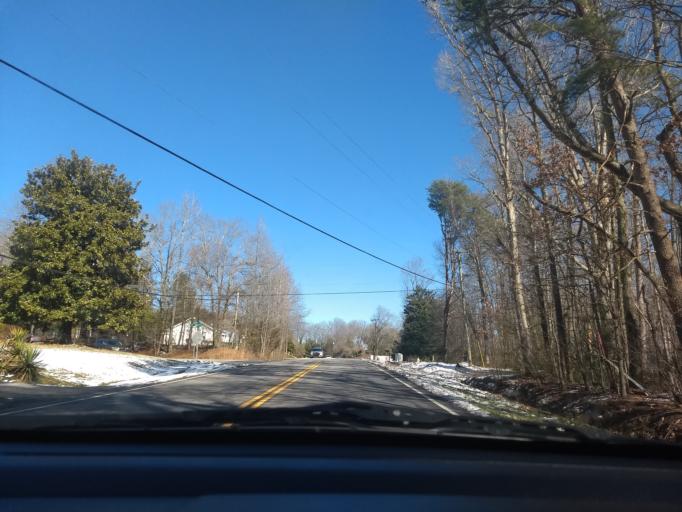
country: US
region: South Carolina
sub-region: Greenville County
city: Wade Hampton
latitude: 34.9084
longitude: -82.3762
